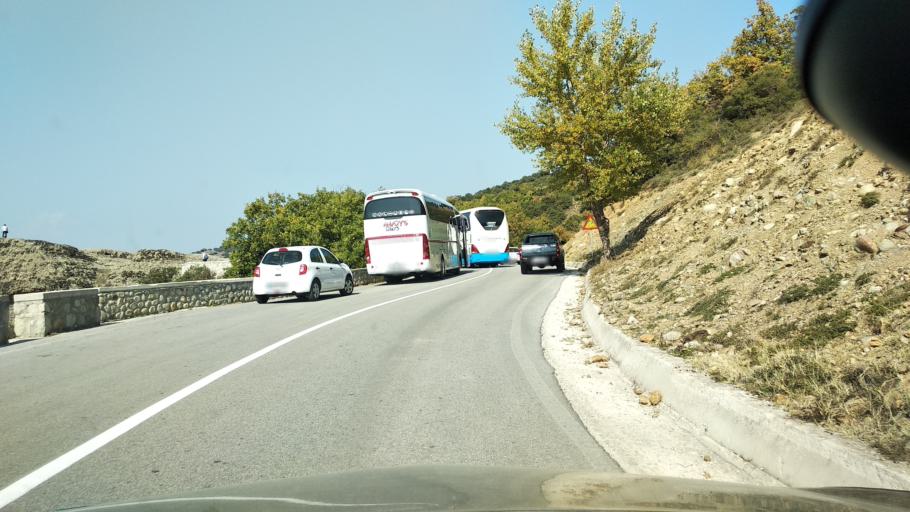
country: GR
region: Thessaly
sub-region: Trikala
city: Kalampaka
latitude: 39.7188
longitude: 21.6375
